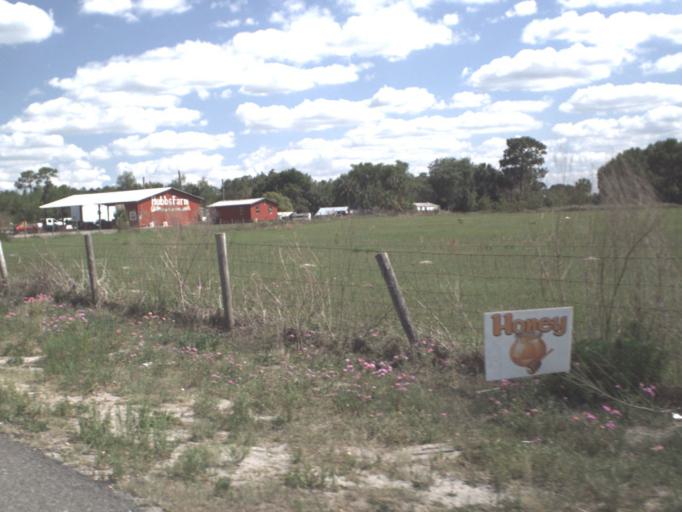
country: US
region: Florida
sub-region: Lake County
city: Mount Plymouth
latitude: 28.8171
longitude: -81.4735
